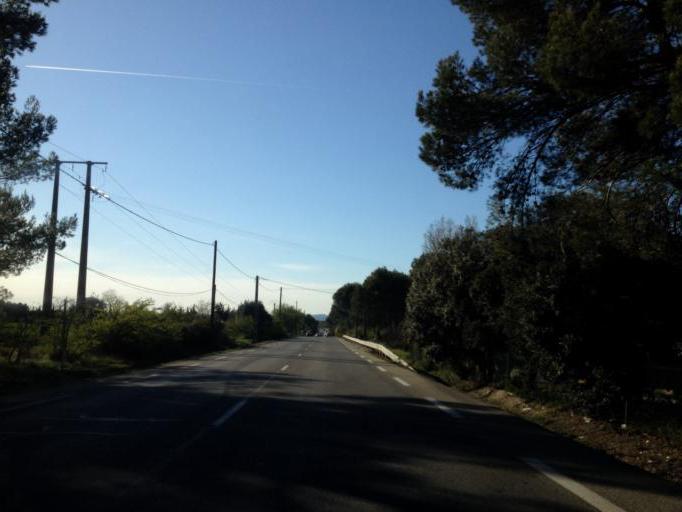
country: FR
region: Provence-Alpes-Cote d'Azur
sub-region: Departement des Bouches-du-Rhone
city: Saint-Cannat
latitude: 43.6075
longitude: 5.3333
